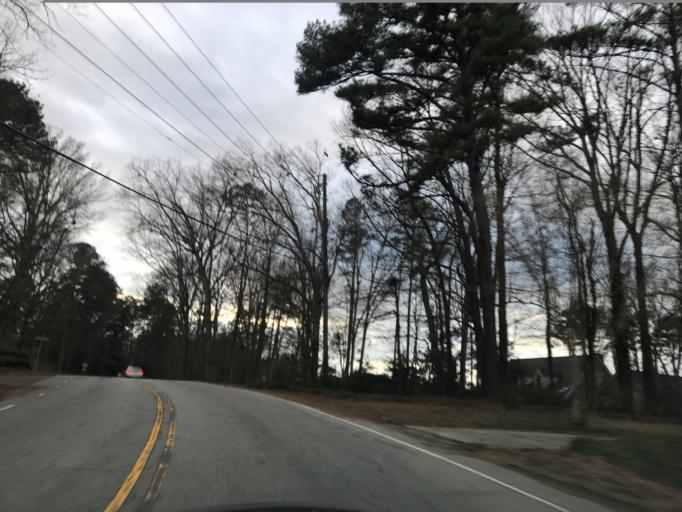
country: US
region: North Carolina
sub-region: Wake County
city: West Raleigh
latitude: 35.8311
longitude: -78.6852
